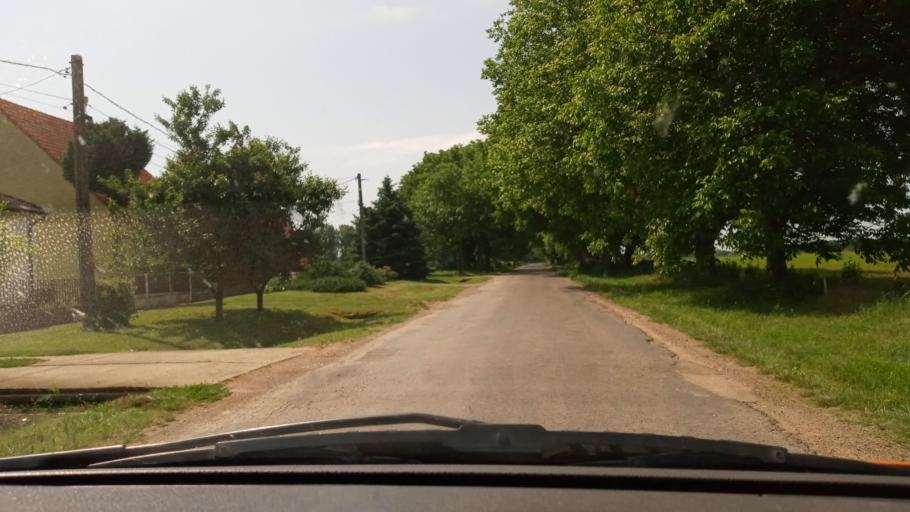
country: HU
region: Baranya
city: Szentlorinc
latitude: 46.0041
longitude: 18.0381
